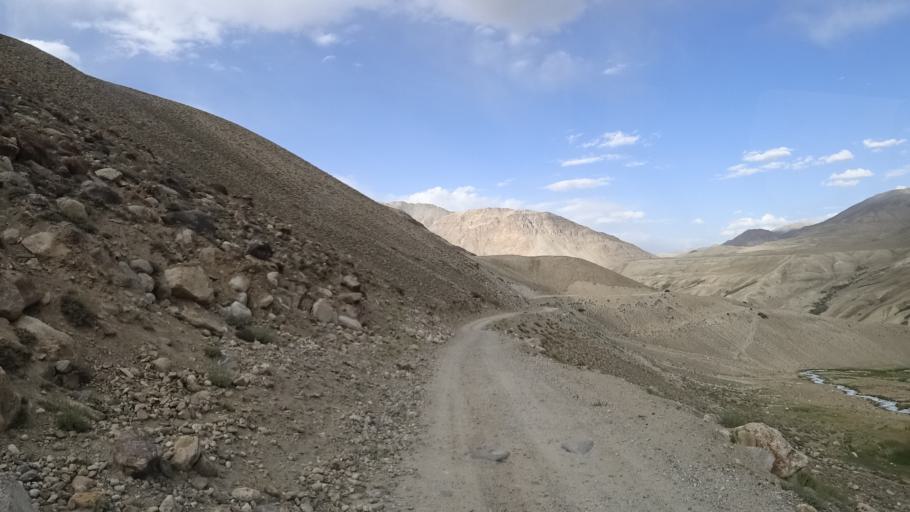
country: AF
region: Badakhshan
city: Khandud
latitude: 37.2207
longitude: 72.7881
